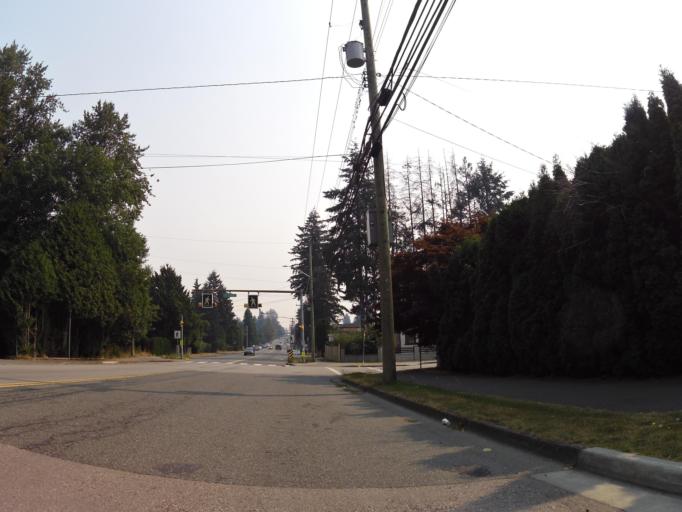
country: CA
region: British Columbia
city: Delta
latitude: 49.1560
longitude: -122.9186
